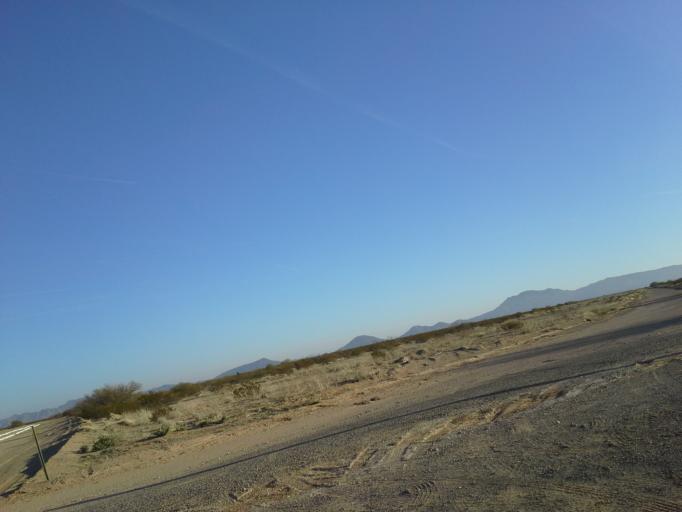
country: US
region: Arizona
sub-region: Pima County
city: Ajo
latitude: 32.6790
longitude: -112.9039
